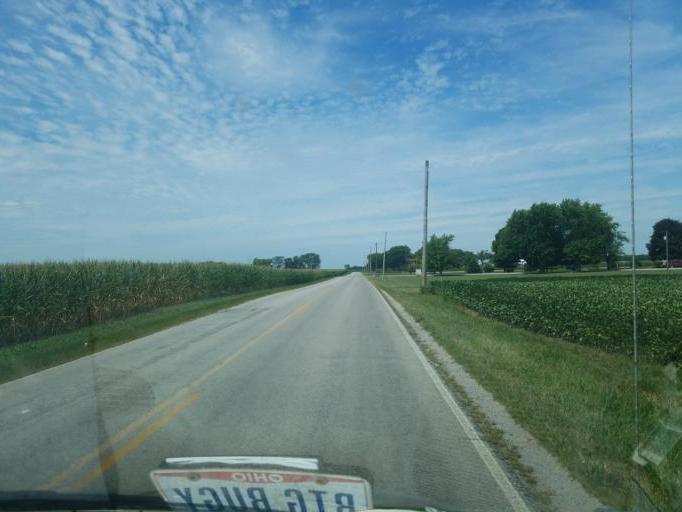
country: US
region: Ohio
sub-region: Madison County
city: West Jefferson
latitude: 39.9544
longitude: -83.2710
